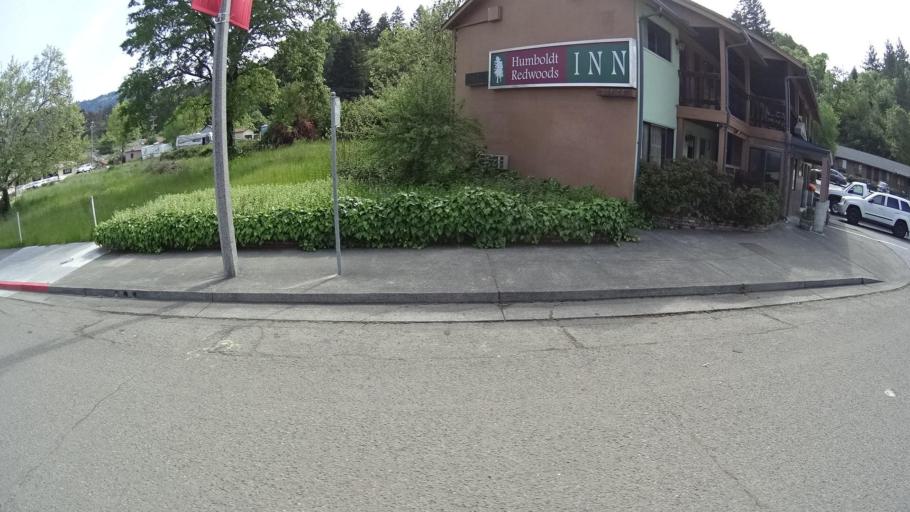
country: US
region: California
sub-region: Humboldt County
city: Redway
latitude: 40.0968
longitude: -123.7952
